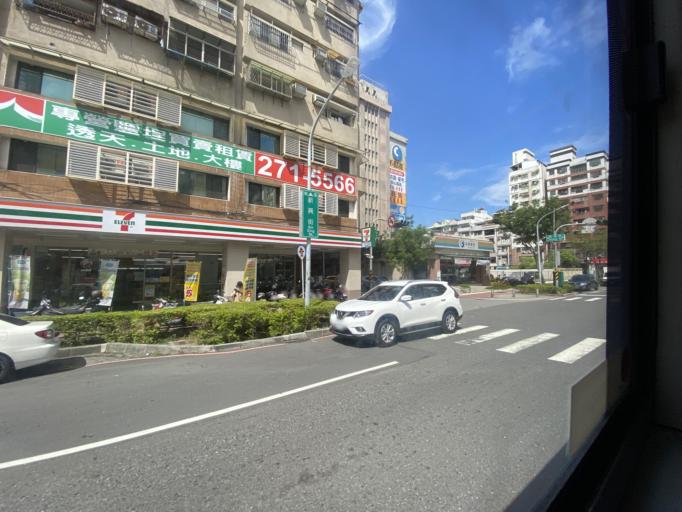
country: TW
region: Kaohsiung
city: Kaohsiung
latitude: 22.6248
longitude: 120.2811
